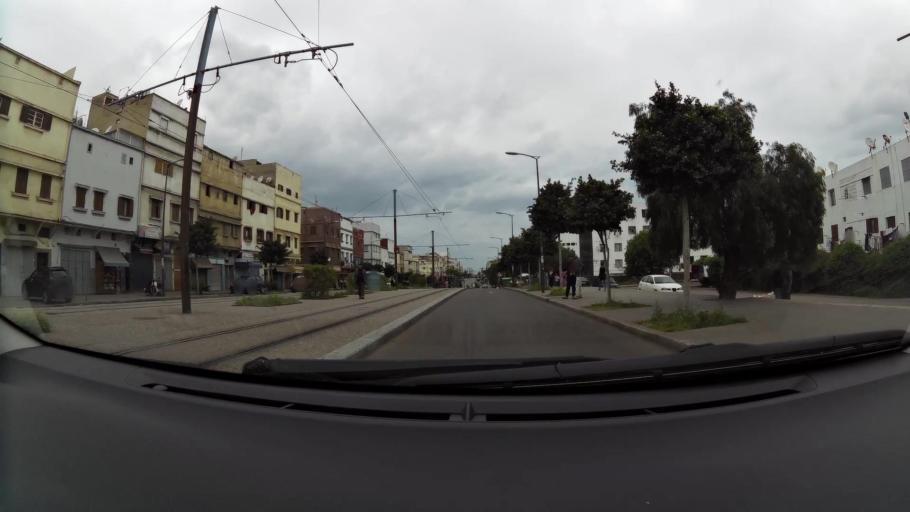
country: MA
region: Grand Casablanca
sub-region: Casablanca
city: Casablanca
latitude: 33.5842
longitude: -7.5660
